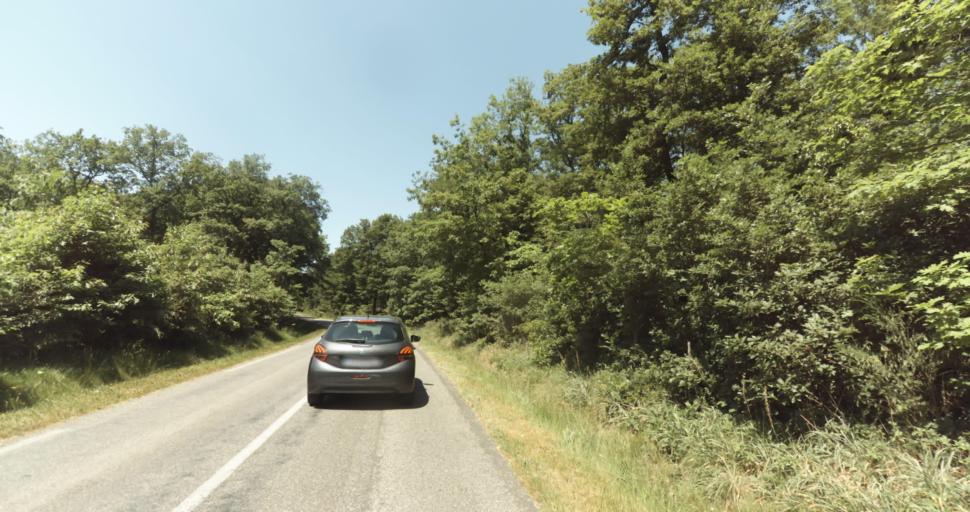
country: FR
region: Midi-Pyrenees
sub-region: Departement de la Haute-Garonne
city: Levignac
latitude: 43.6217
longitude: 1.1896
